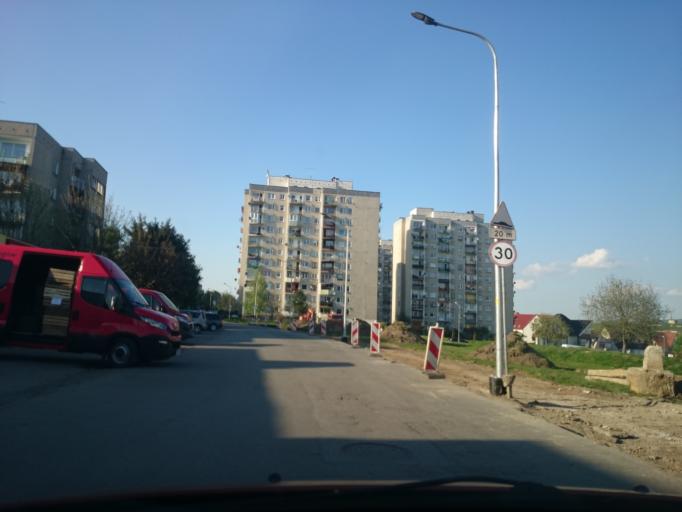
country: PL
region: Lower Silesian Voivodeship
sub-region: Powiat klodzki
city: Klodzko
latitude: 50.4343
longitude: 16.6409
